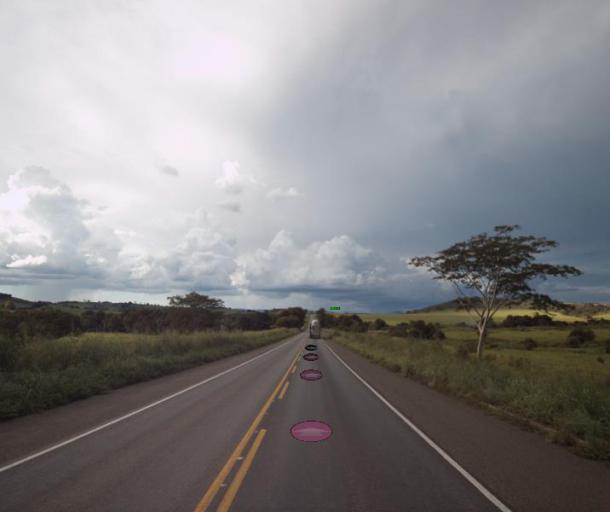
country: BR
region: Goias
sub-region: Ceres
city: Ceres
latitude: -15.2364
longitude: -49.5559
